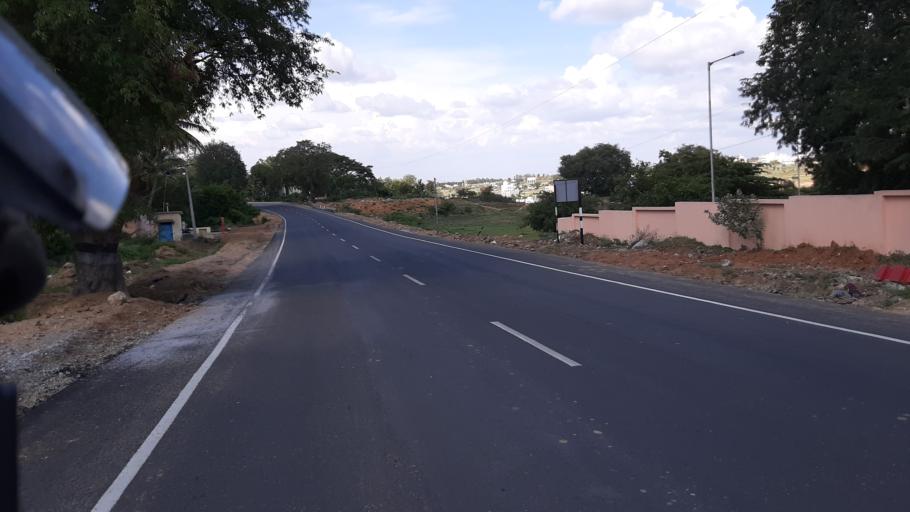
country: IN
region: Tamil Nadu
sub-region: Krishnagiri
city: Denkanikota
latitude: 12.5355
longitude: 77.7879
